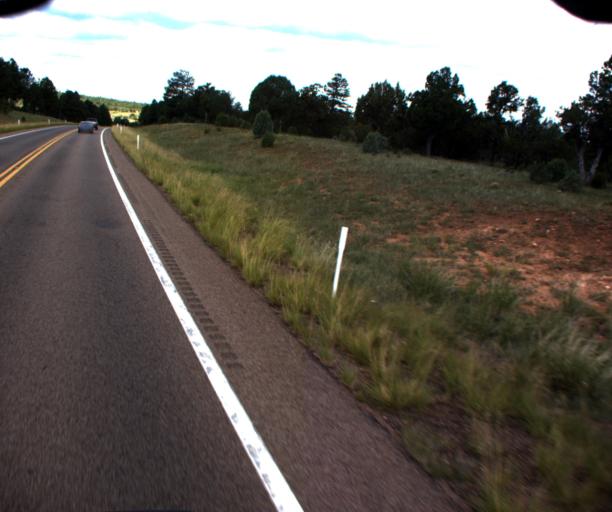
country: US
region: Arizona
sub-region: Navajo County
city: Heber-Overgaard
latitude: 34.3818
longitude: -110.4873
